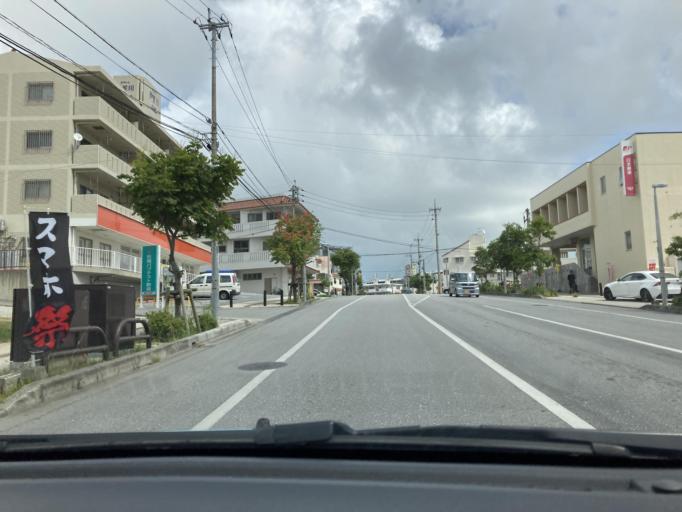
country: JP
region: Okinawa
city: Ginowan
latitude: 26.2276
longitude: 127.7296
